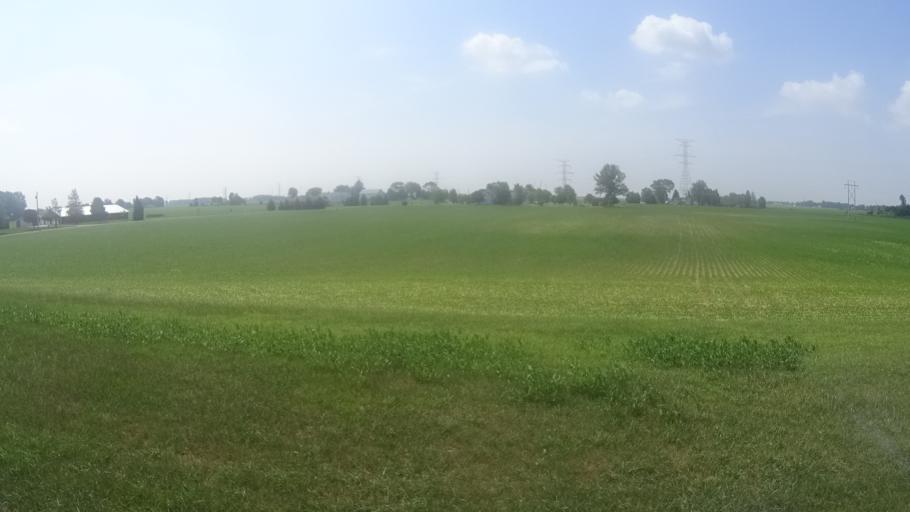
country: US
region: Ohio
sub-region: Erie County
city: Sandusky
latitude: 41.3583
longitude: -82.7160
